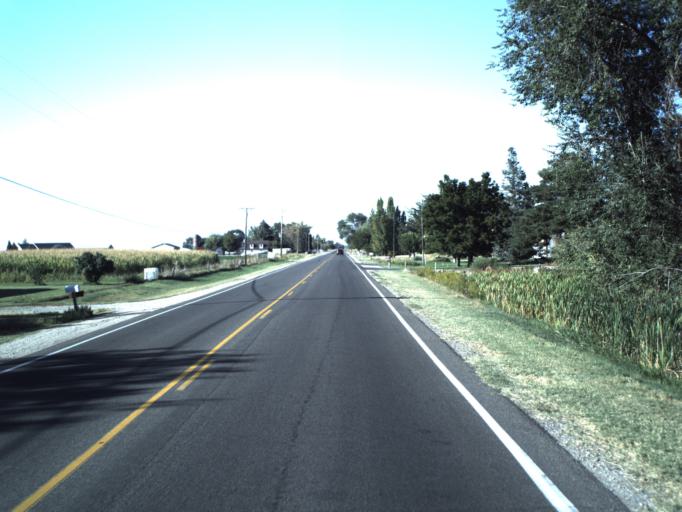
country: US
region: Utah
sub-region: Weber County
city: Hooper
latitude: 41.1792
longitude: -112.1226
